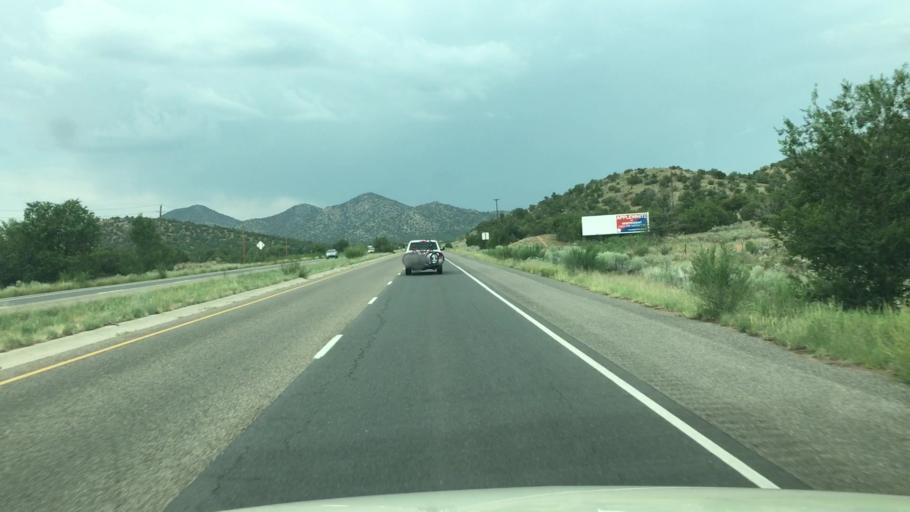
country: US
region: New Mexico
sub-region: Santa Fe County
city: Eldorado at Santa Fe
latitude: 35.5428
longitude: -105.8845
